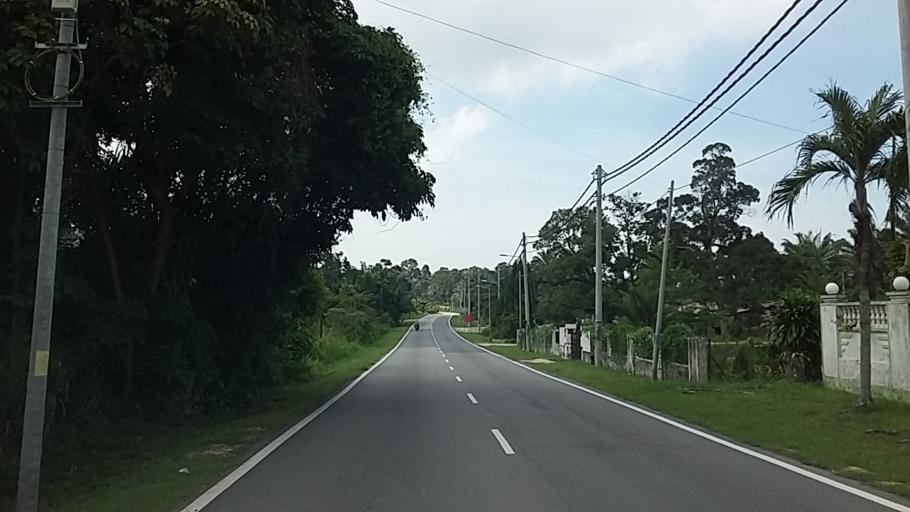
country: MY
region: Johor
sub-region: Daerah Batu Pahat
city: Batu Pahat
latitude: 1.7912
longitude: 102.8973
